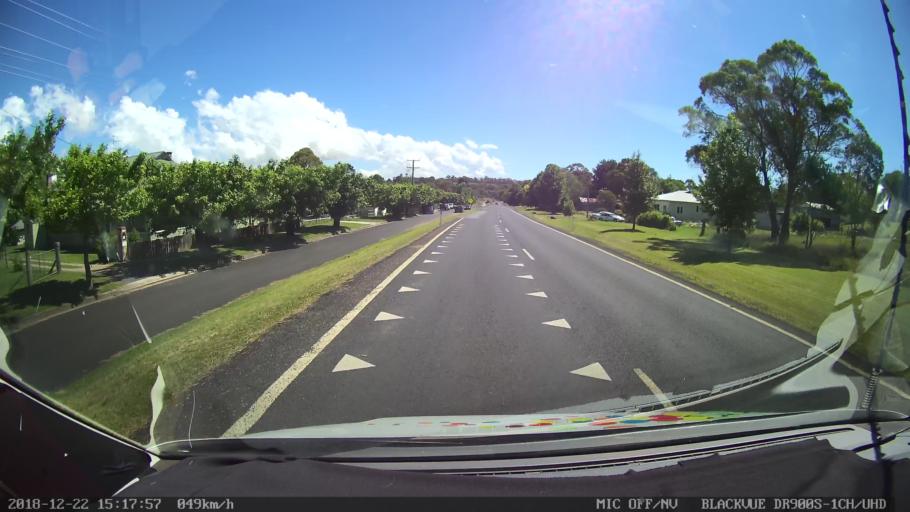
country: AU
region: New South Wales
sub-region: Bellingen
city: Dorrigo
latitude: -30.4009
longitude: 152.3505
